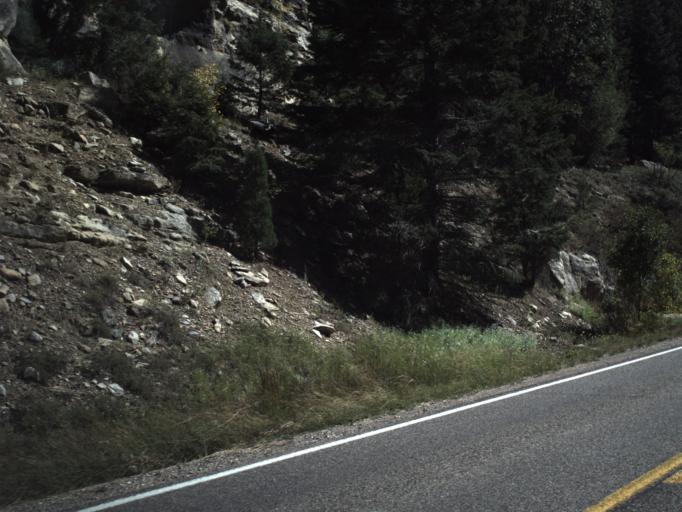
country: US
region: Utah
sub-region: Iron County
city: Cedar City
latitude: 37.6226
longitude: -112.9328
